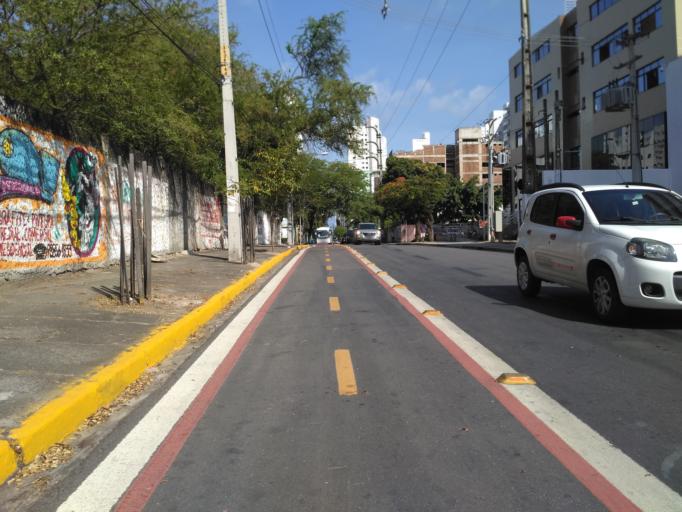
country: BR
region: Pernambuco
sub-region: Recife
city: Recife
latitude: -8.1412
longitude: -34.9110
